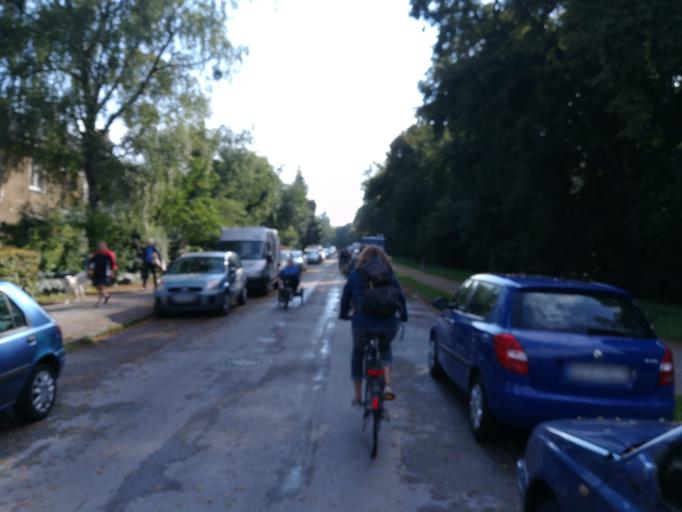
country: DE
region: Bavaria
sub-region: Upper Bavaria
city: Munich
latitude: 48.1659
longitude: 11.5310
